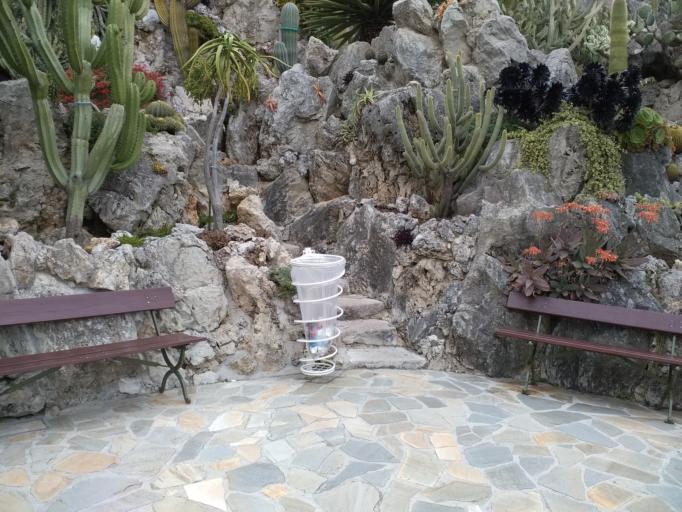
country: MC
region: Commune de Monaco
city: Monaco
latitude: 43.7309
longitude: 7.4135
